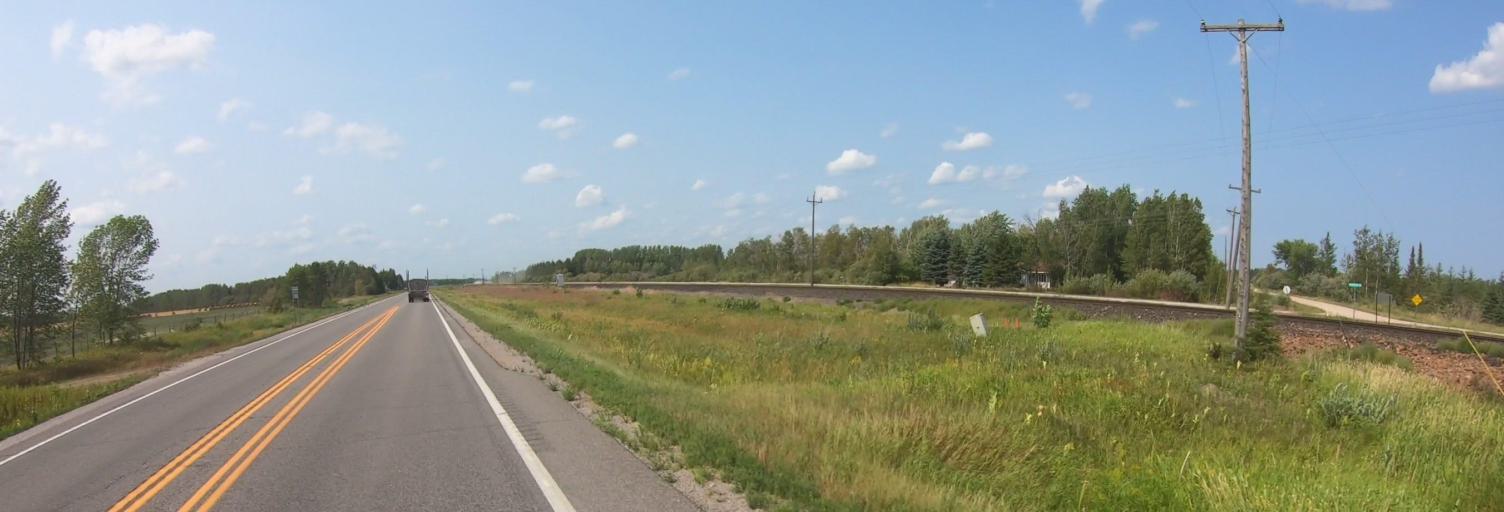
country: US
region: Minnesota
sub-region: Roseau County
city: Warroad
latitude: 48.8708
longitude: -95.2649
